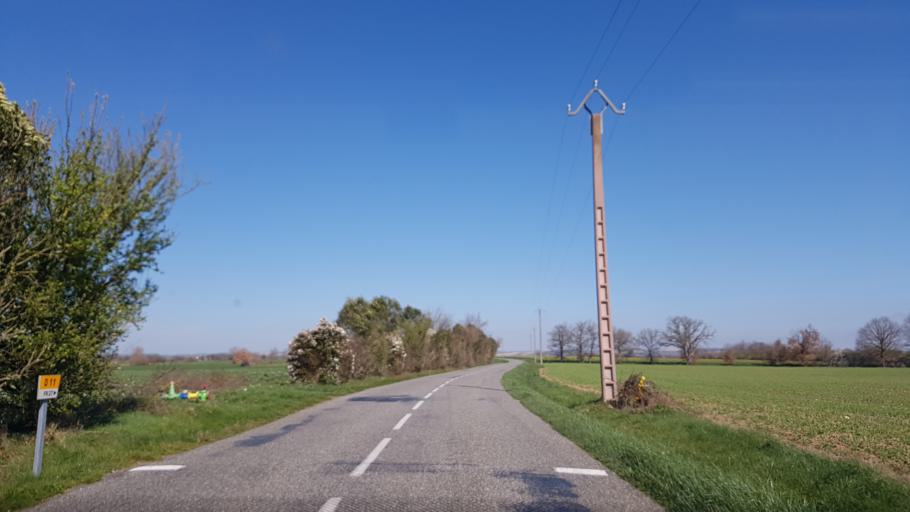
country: FR
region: Languedoc-Roussillon
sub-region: Departement de l'Aude
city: Belpech
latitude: 43.1619
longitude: 1.7094
